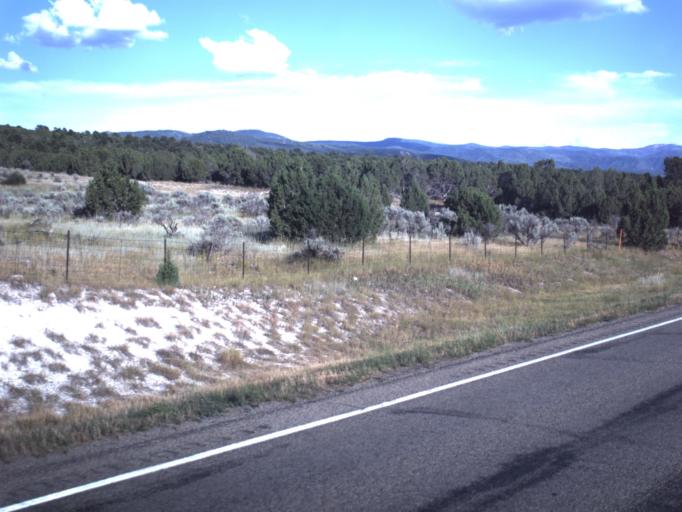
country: US
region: Utah
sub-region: Sanpete County
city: Fairview
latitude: 39.6720
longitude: -111.4556
